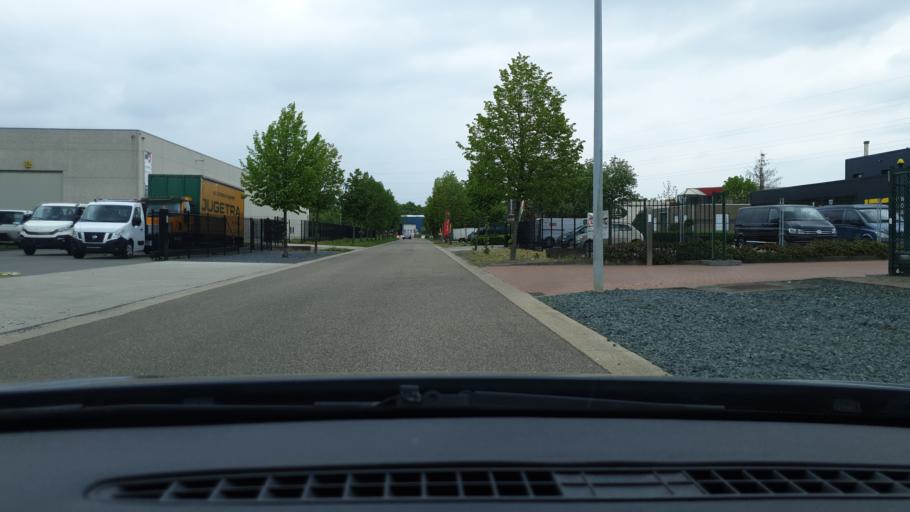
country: BE
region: Flanders
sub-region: Provincie Antwerpen
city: Balen
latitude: 51.1611
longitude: 5.1525
